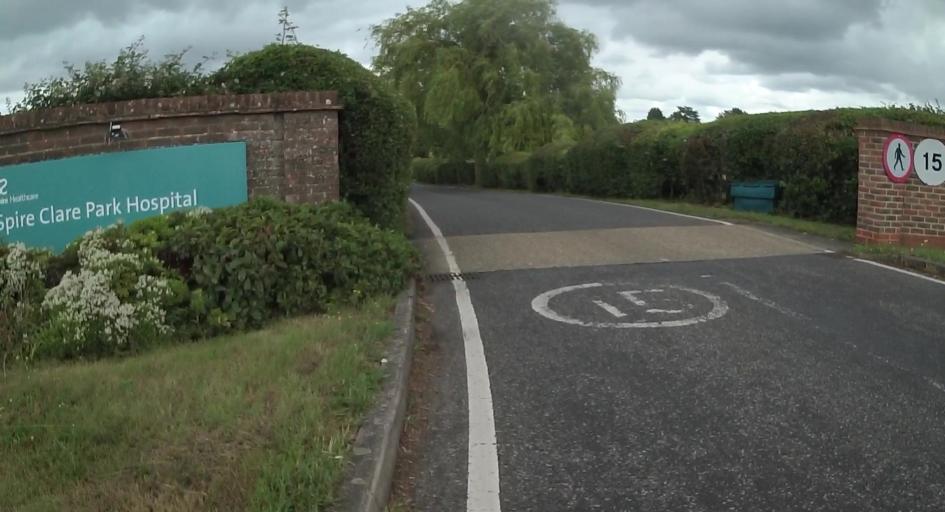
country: GB
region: England
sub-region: Surrey
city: Farnham
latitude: 51.2250
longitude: -0.8523
